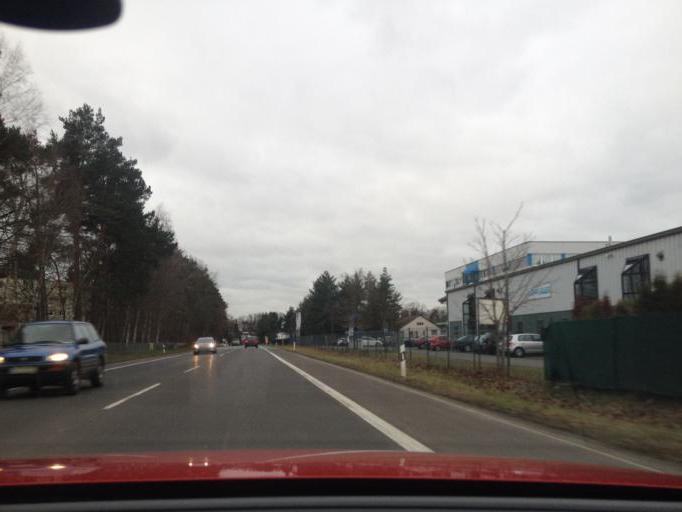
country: DE
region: Bavaria
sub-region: Regierungsbezirk Mittelfranken
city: Ruckersdorf
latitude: 49.4917
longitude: 11.2524
